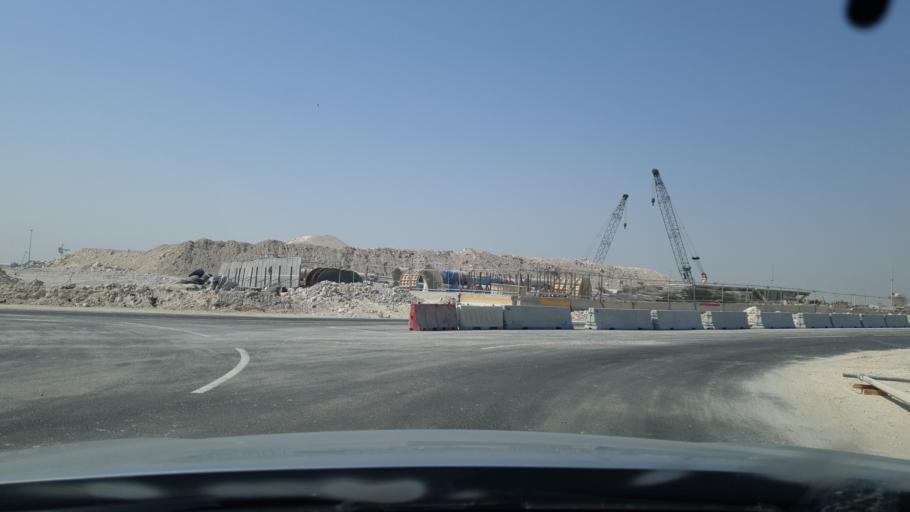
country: QA
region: Baladiyat ad Dawhah
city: Doha
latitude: 25.2234
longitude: 51.5257
